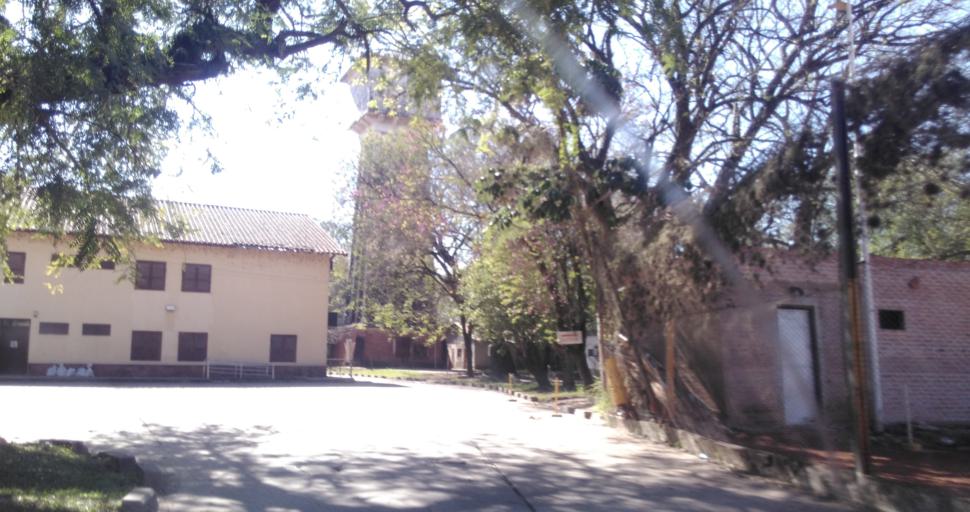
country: AR
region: Chaco
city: Resistencia
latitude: -27.4646
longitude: -58.9825
